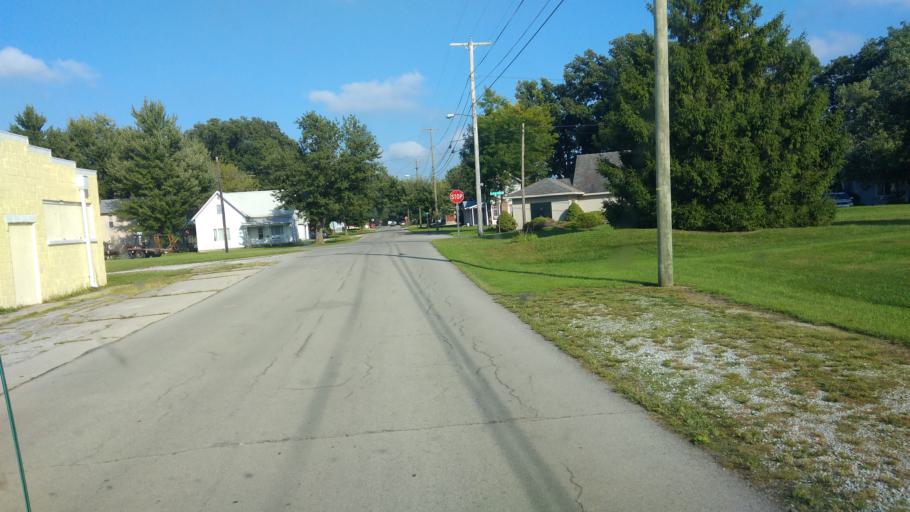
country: US
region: Ohio
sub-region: Hardin County
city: Forest
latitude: 40.7997
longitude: -83.5144
